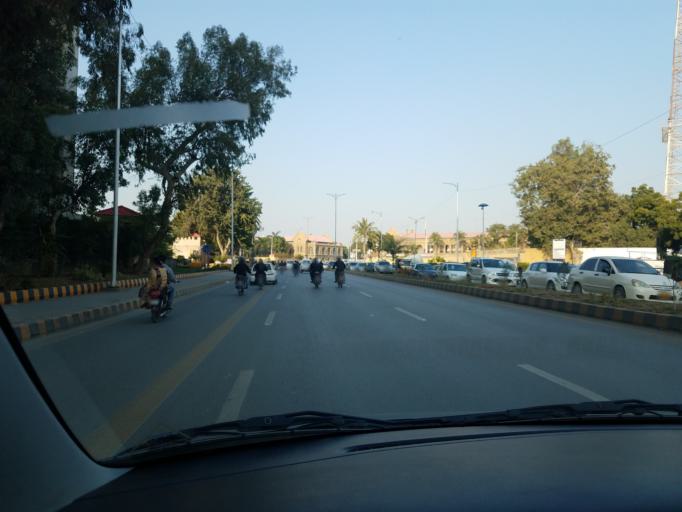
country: PK
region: Sindh
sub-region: Karachi District
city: Karachi
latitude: 24.8533
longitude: 67.0350
